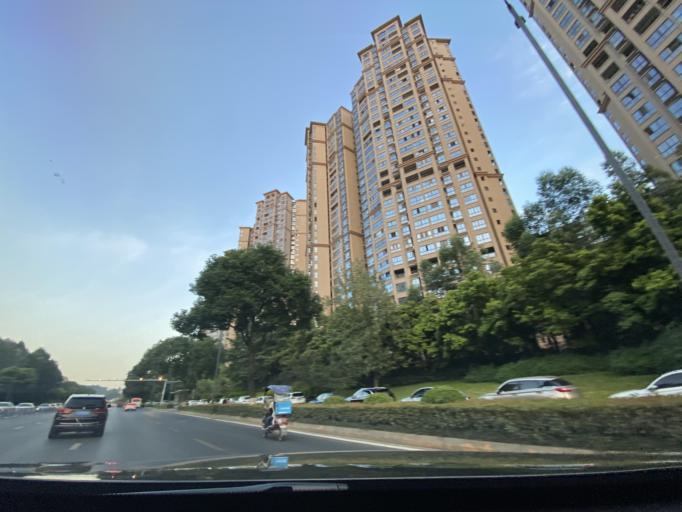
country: CN
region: Sichuan
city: Longquan
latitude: 30.5843
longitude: 104.2926
